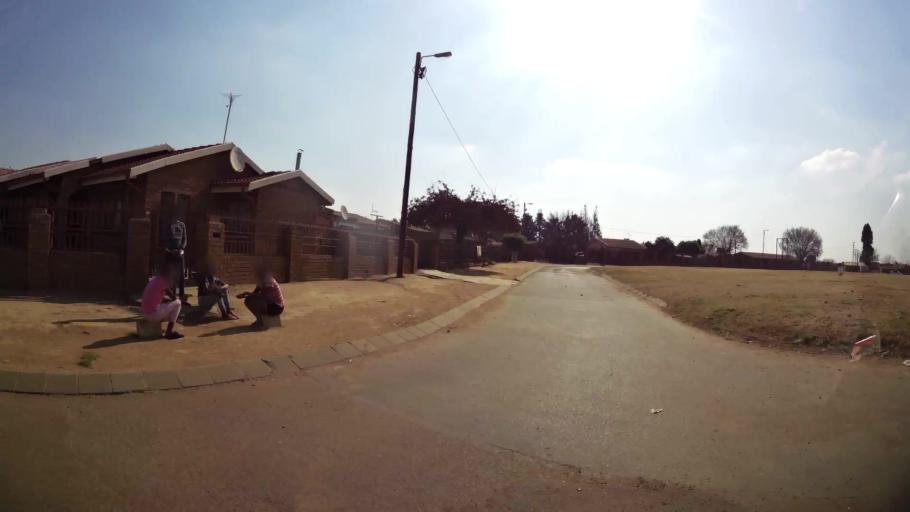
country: ZA
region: Gauteng
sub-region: Ekurhuleni Metropolitan Municipality
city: Brakpan
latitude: -26.1348
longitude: 28.4298
